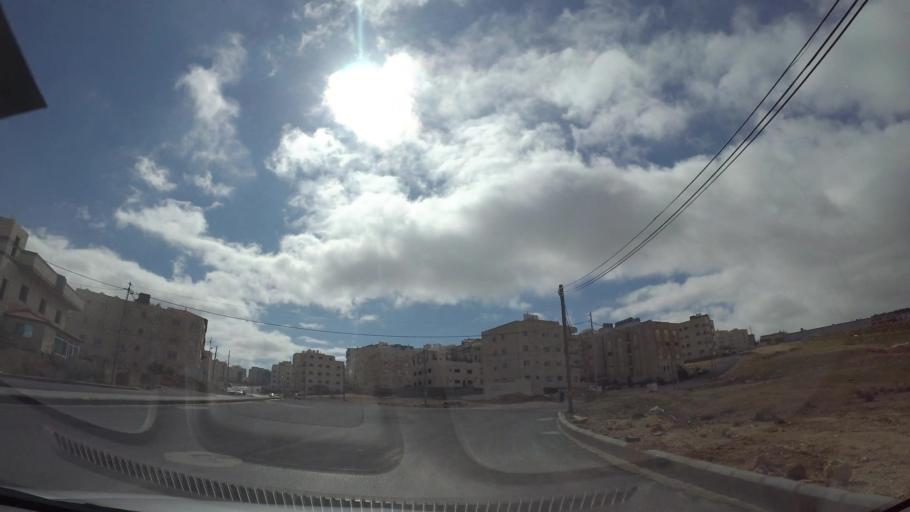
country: JO
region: Amman
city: Al Jubayhah
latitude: 32.0645
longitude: 35.8878
